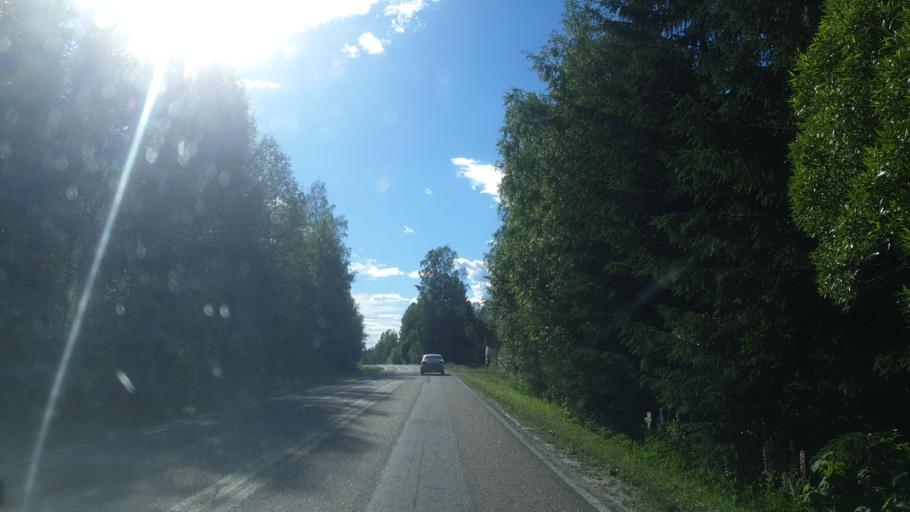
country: FI
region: Southern Savonia
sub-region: Mikkeli
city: Pertunmaa
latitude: 61.5220
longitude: 26.5672
